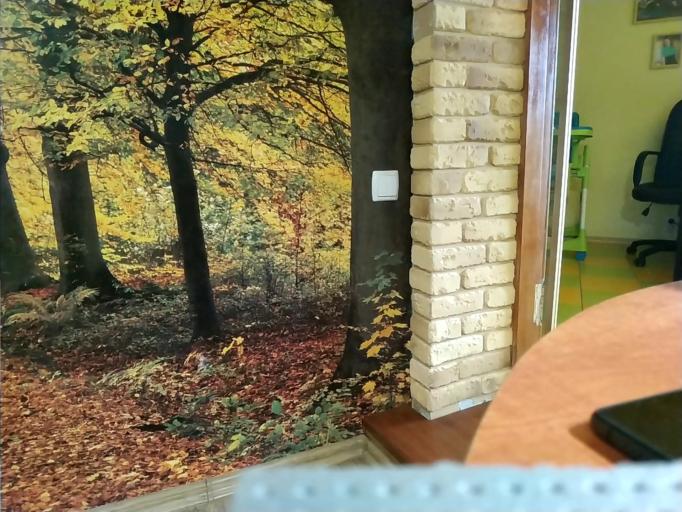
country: RU
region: Vladimir
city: Bavleny
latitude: 56.3656
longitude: 39.5352
